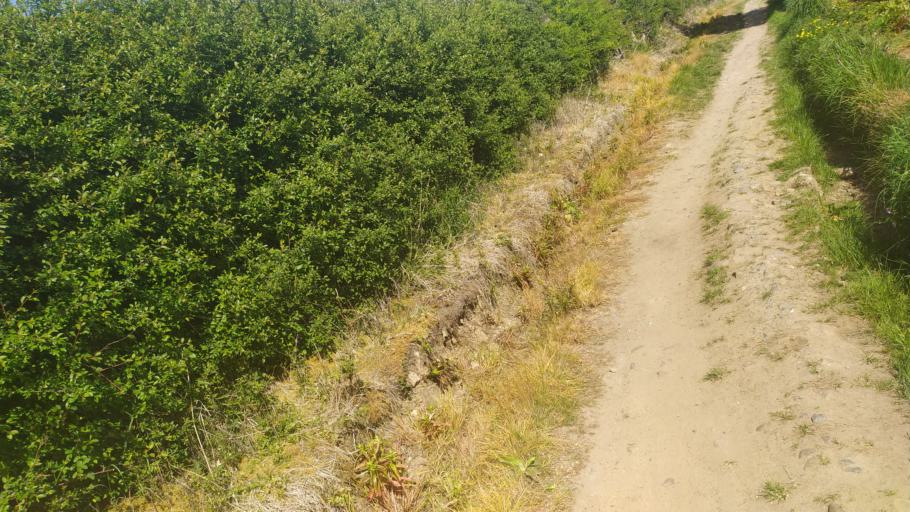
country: GB
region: England
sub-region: City and Borough of Leeds
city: Chapel Allerton
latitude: 53.8783
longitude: -1.5585
